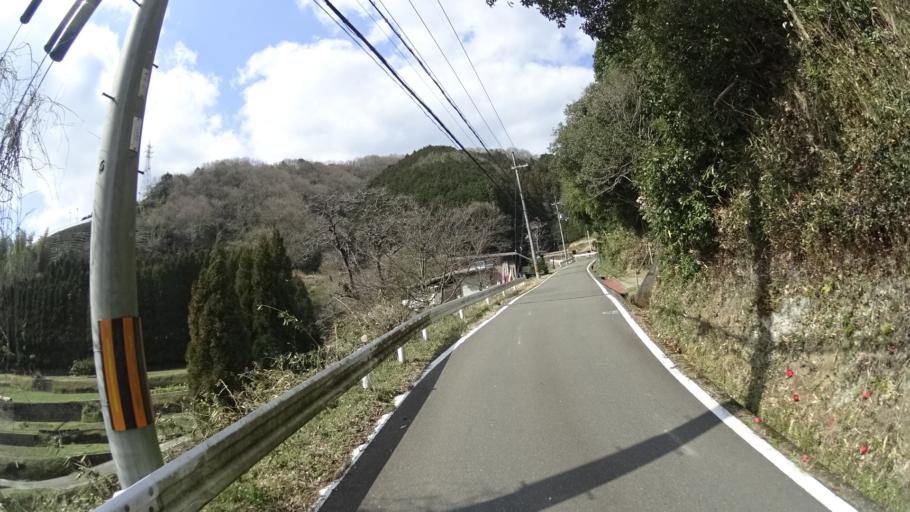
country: JP
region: Nara
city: Nara-shi
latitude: 34.7675
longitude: 135.9096
